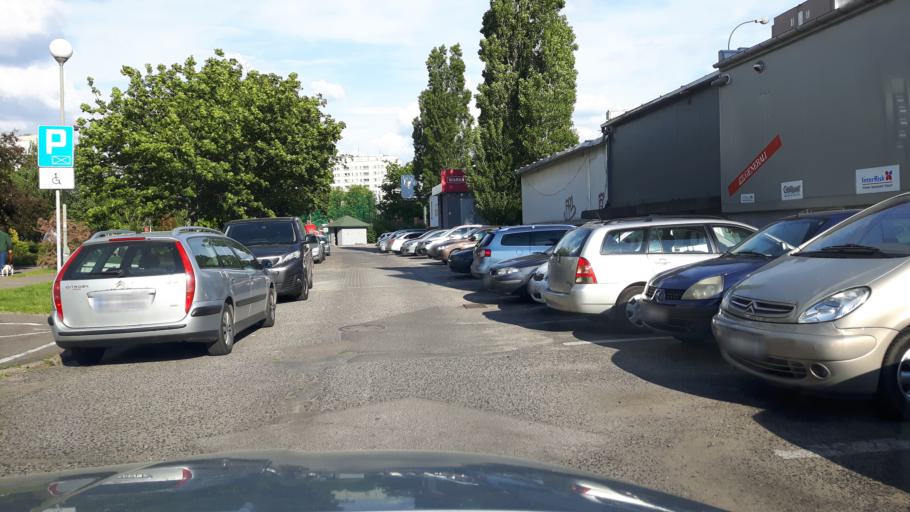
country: PL
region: Masovian Voivodeship
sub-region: Warszawa
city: Praga Poludnie
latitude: 52.2270
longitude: 21.0983
